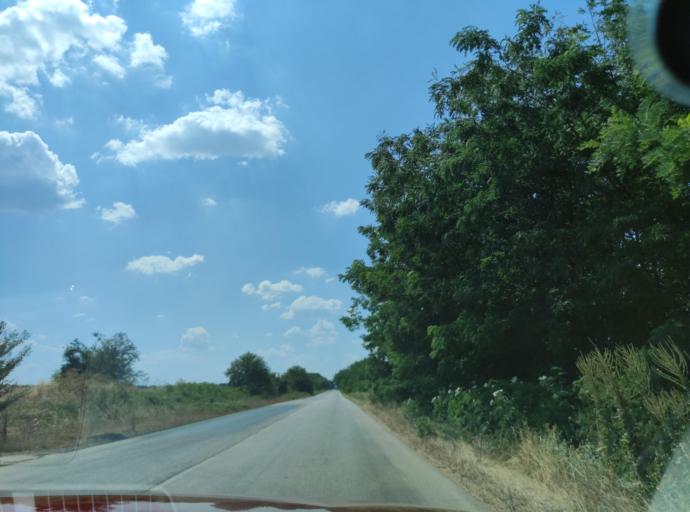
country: BG
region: Pleven
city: Iskur
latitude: 43.4521
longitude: 24.2985
